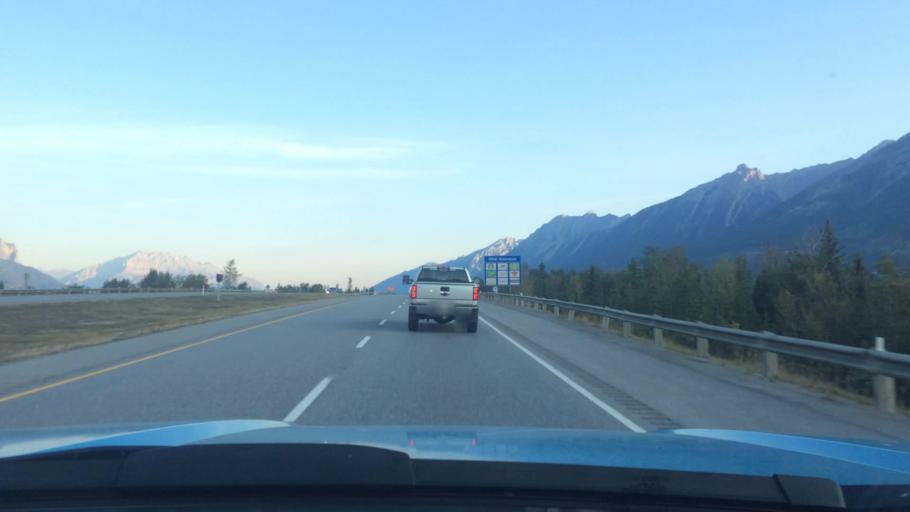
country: CA
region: Alberta
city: Canmore
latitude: 51.0724
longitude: -115.3291
